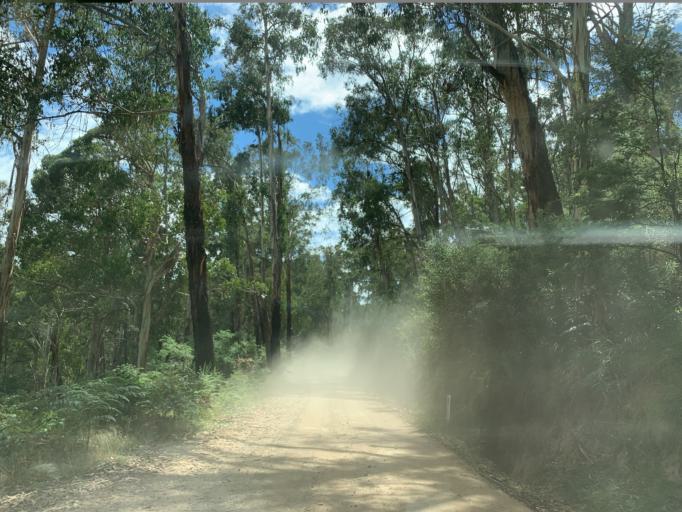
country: AU
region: Victoria
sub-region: Mansfield
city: Mansfield
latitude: -37.0931
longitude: 146.5157
